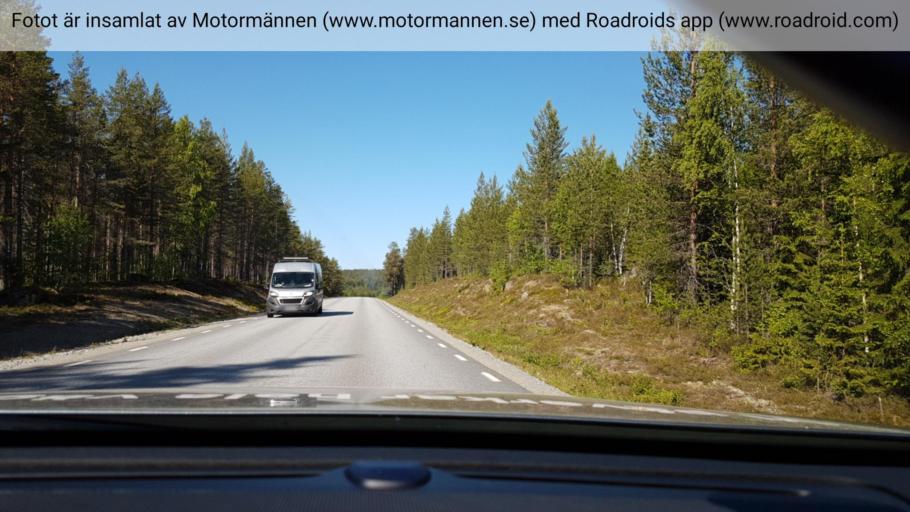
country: SE
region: Vaesterbotten
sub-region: Bjurholms Kommun
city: Bjurholm
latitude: 64.0009
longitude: 18.7572
